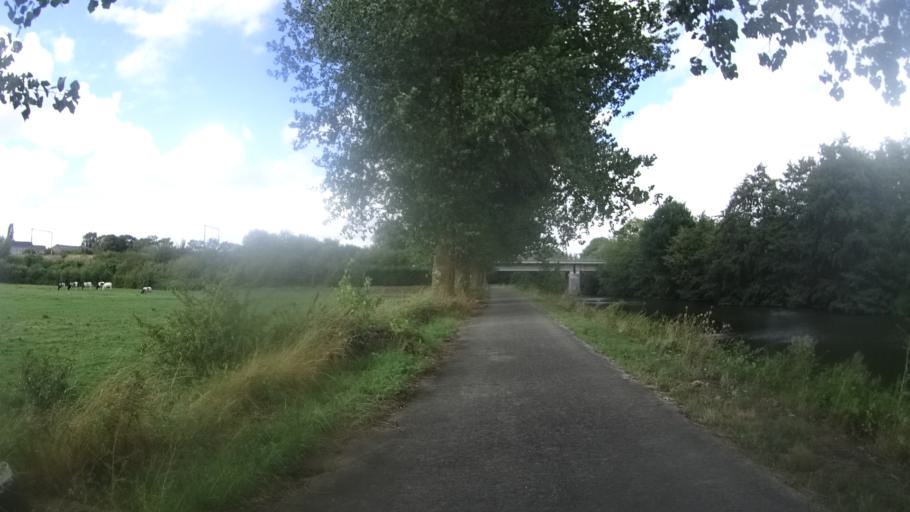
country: BE
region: Wallonia
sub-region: Province du Hainaut
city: Merbes-le-Chateau
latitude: 50.3110
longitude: 4.1503
